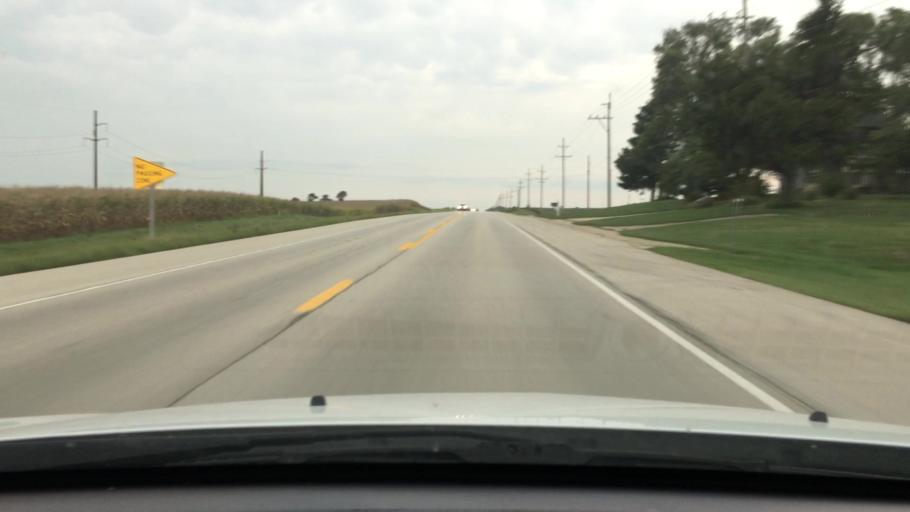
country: US
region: Illinois
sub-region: DeKalb County
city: Waterman
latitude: 41.8311
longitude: -88.7540
